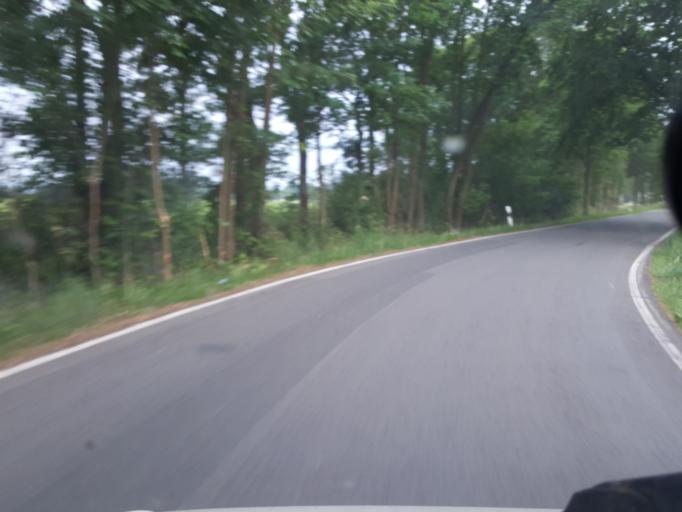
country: DE
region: North Rhine-Westphalia
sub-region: Regierungsbezirk Detmold
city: Minden
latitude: 52.3646
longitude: 8.8610
